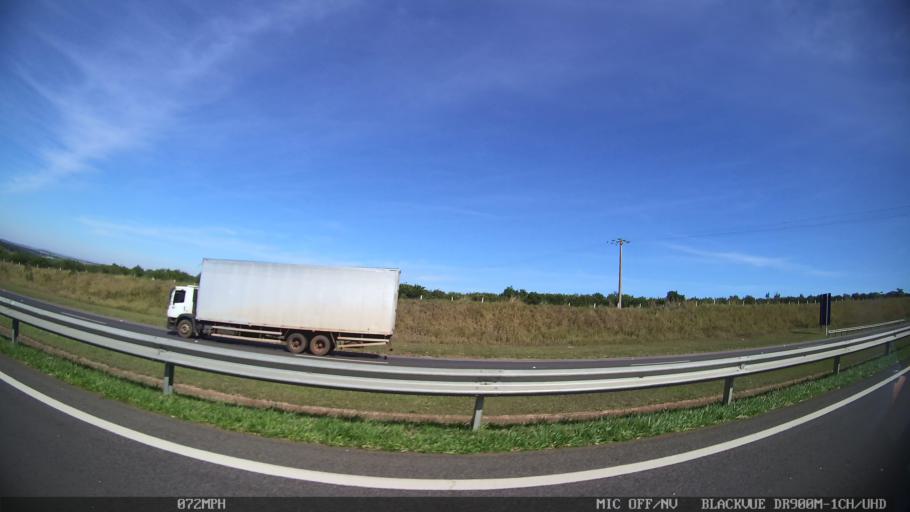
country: BR
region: Sao Paulo
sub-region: Porto Ferreira
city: Porto Ferreira
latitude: -21.7862
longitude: -47.5250
